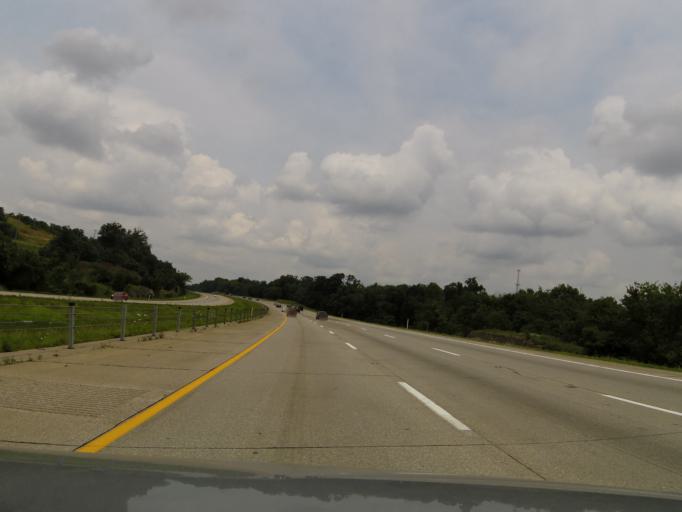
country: US
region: Kentucky
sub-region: Bullitt County
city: Shepherdsville
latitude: 38.0090
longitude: -85.6980
